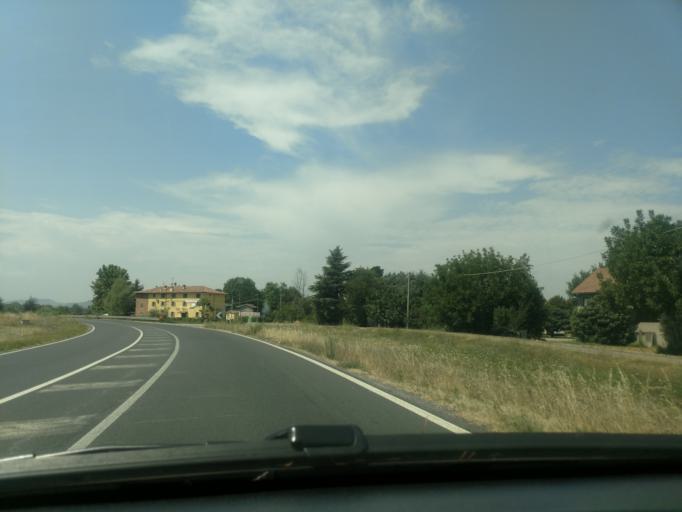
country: IT
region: Emilia-Romagna
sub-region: Provincia di Bologna
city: Villanova
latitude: 44.4836
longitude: 11.4507
